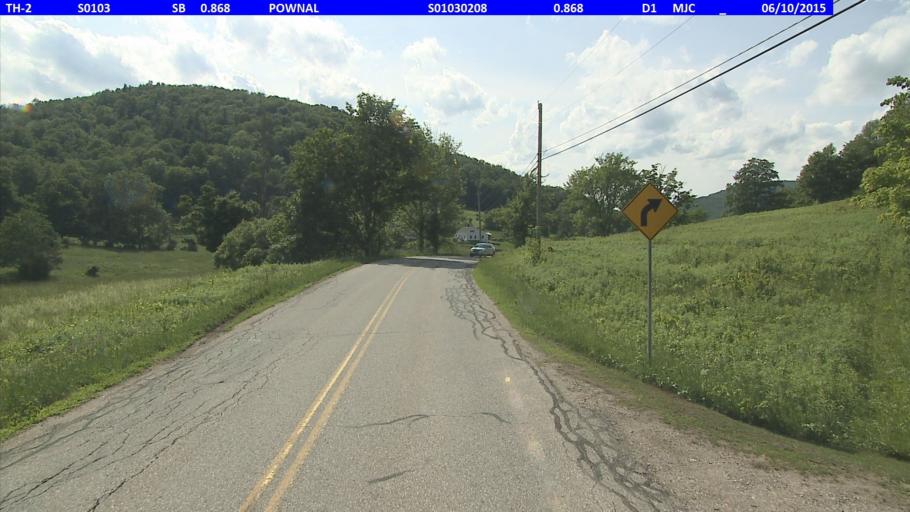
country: US
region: Vermont
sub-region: Bennington County
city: Bennington
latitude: 42.8022
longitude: -73.2529
